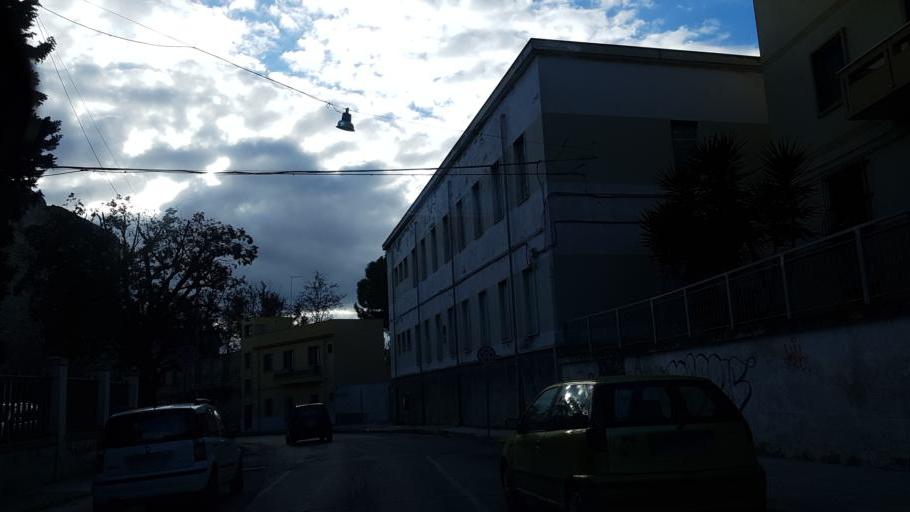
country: IT
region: Apulia
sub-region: Provincia di Brindisi
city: Brindisi
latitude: 40.6322
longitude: 17.9417
